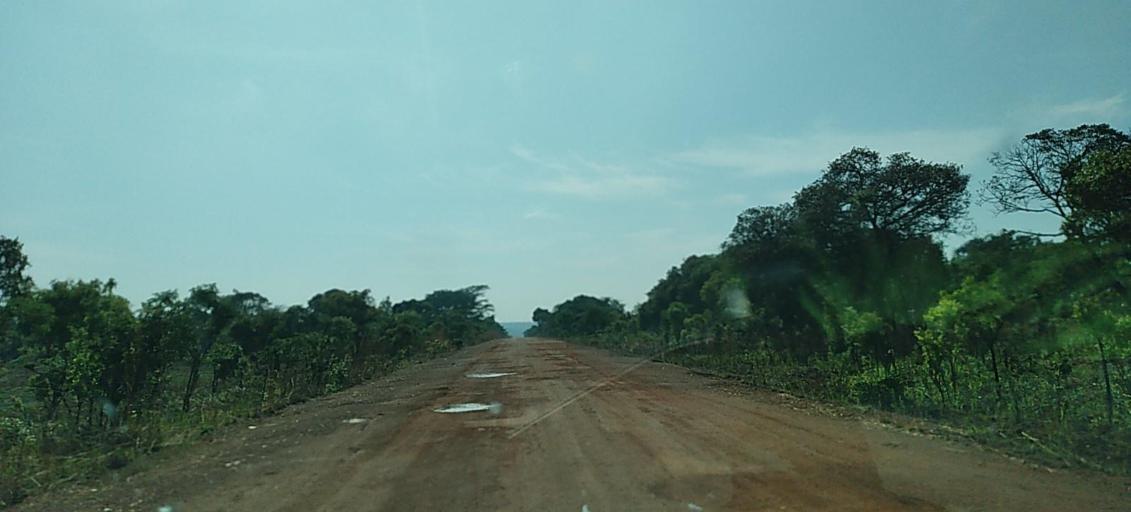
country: ZM
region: North-Western
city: Mwinilunga
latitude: -11.8216
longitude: 25.1003
